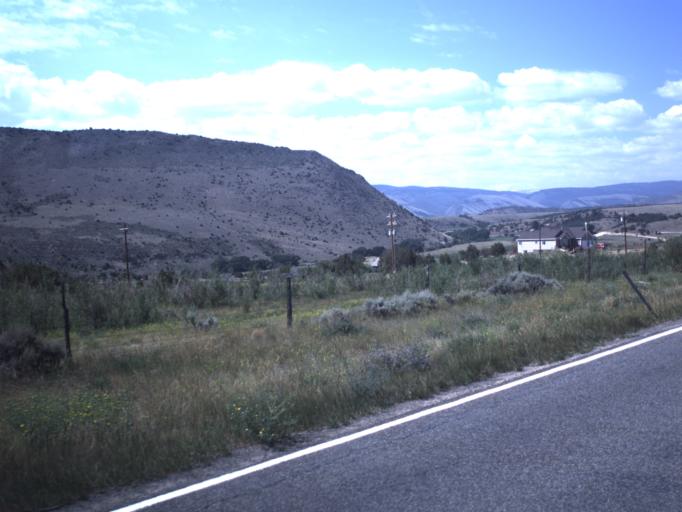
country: US
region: Utah
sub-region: Daggett County
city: Manila
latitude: 40.9779
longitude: -109.8166
